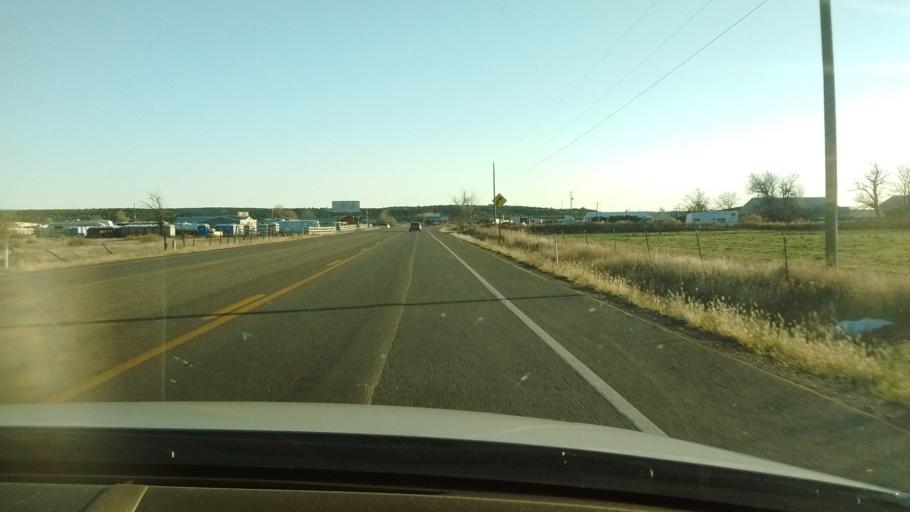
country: US
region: Utah
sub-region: Kane County
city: Kanab
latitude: 37.0159
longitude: -112.5250
